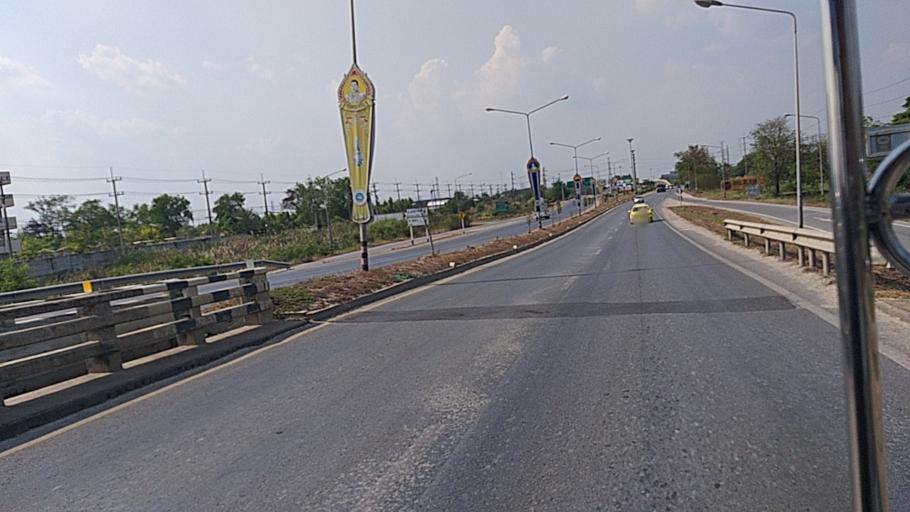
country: TH
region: Pathum Thani
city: Sam Khok
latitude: 14.0843
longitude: 100.5200
